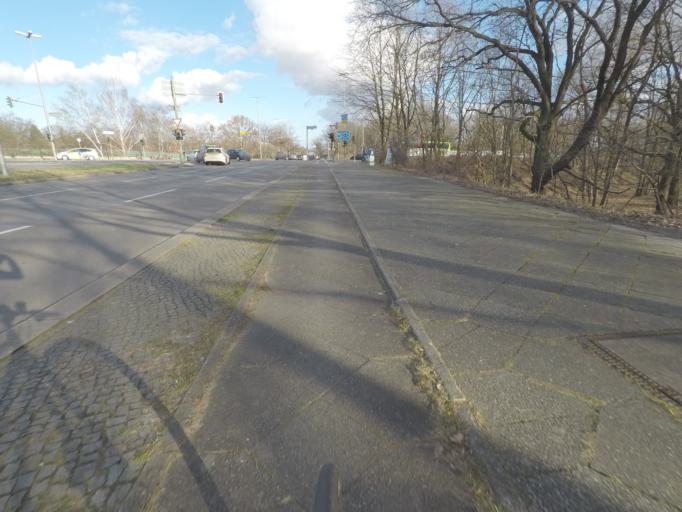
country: DE
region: Berlin
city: Charlottenburg-Nord
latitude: 52.5479
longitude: 13.2960
